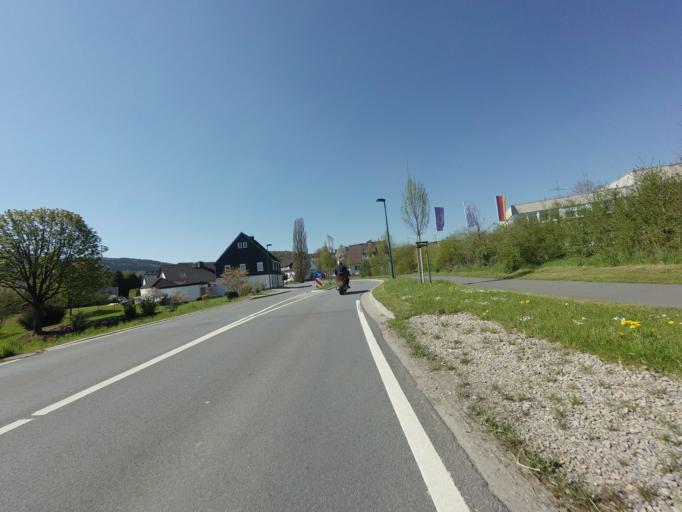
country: DE
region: North Rhine-Westphalia
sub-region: Regierungsbezirk Arnsberg
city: Attendorn
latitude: 51.1074
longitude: 7.9573
